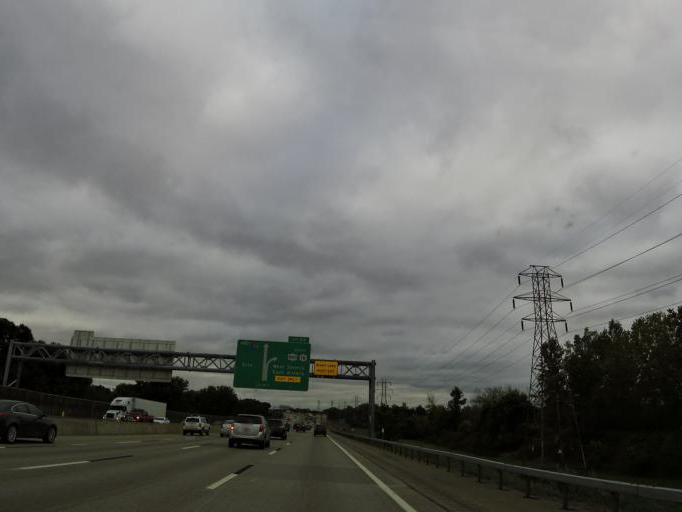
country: US
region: New York
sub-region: Erie County
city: West Seneca
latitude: 42.8634
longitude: -78.7921
